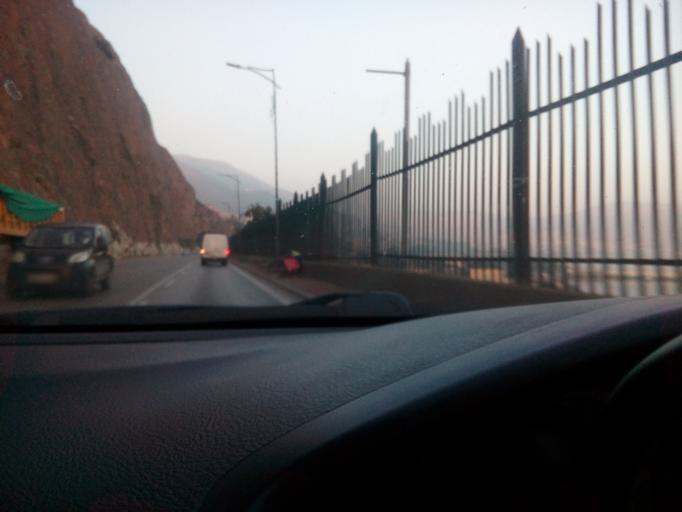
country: DZ
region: Oran
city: Mers el Kebir
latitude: 35.7120
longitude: -0.6796
